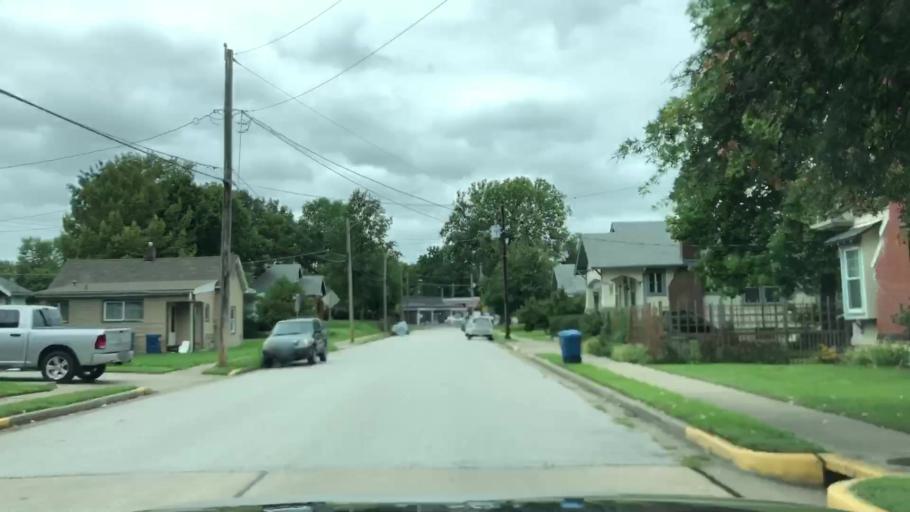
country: US
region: Missouri
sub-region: Saint Charles County
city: Saint Charles
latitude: 38.7864
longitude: -90.4913
